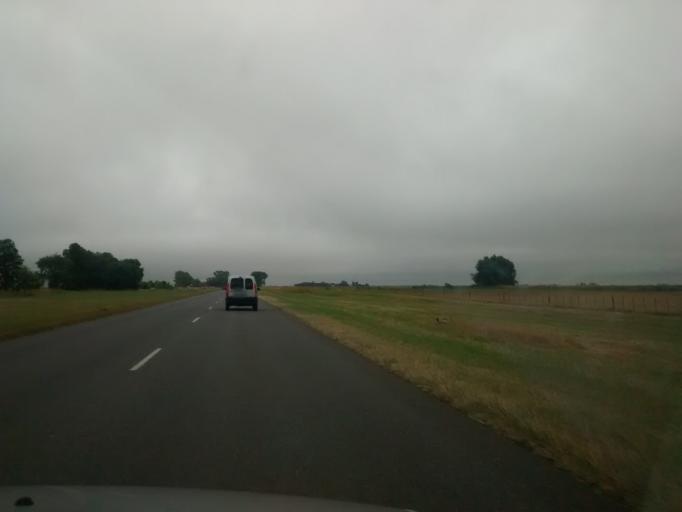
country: AR
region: Buenos Aires
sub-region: Partido de Ayacucho
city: Ayacucho
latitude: -37.2422
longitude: -58.4898
